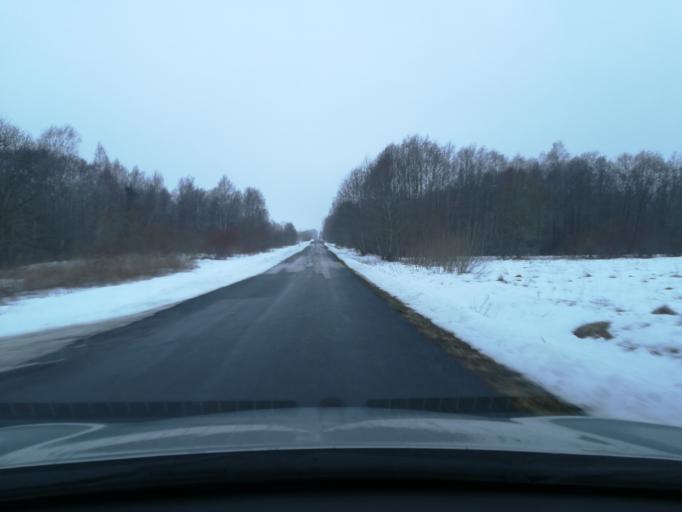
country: EE
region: Harju
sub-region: Raasiku vald
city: Raasiku
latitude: 59.3411
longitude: 25.2283
